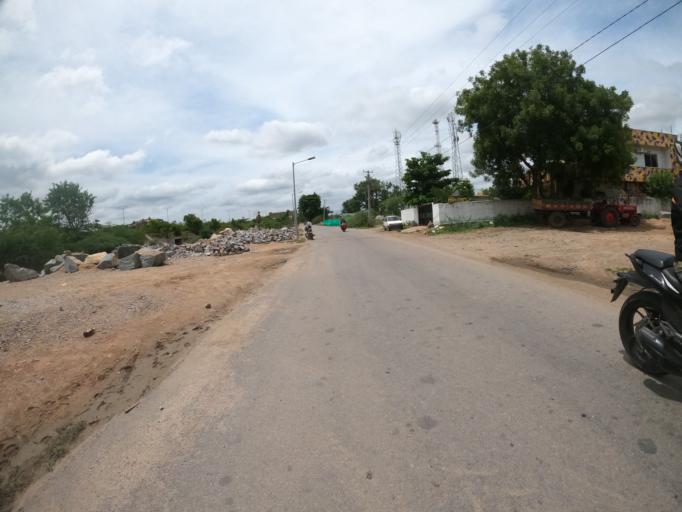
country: IN
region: Telangana
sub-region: Hyderabad
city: Hyderabad
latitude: 17.2975
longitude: 78.3789
